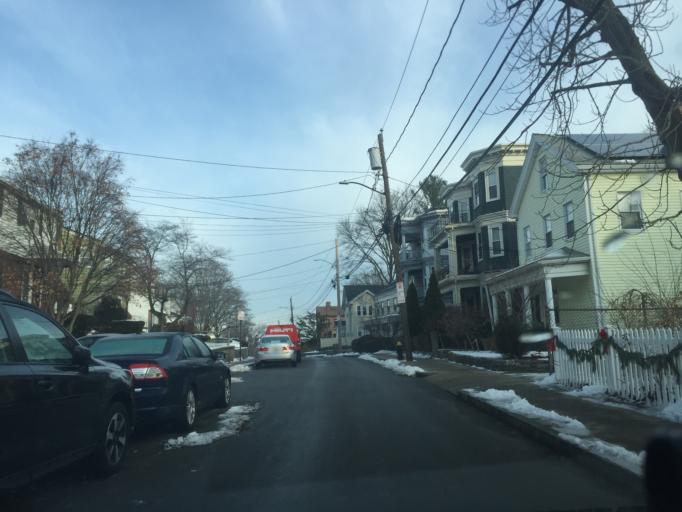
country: US
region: Massachusetts
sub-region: Middlesex County
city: Watertown
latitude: 42.3496
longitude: -71.1578
